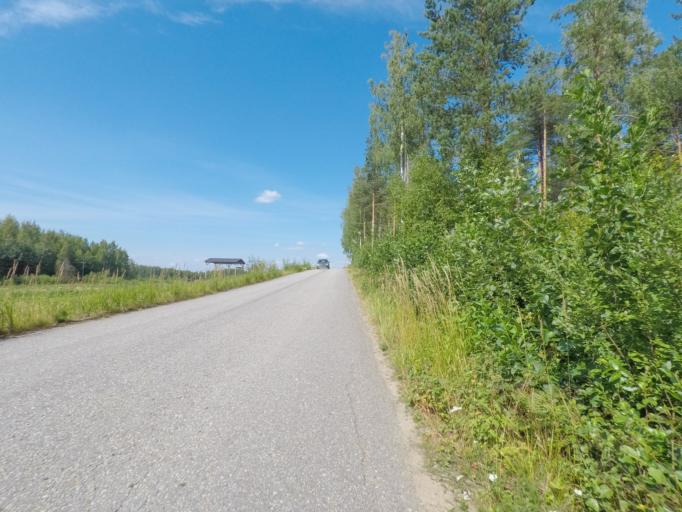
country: FI
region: Southern Savonia
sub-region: Mikkeli
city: Puumala
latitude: 61.4131
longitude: 28.0922
